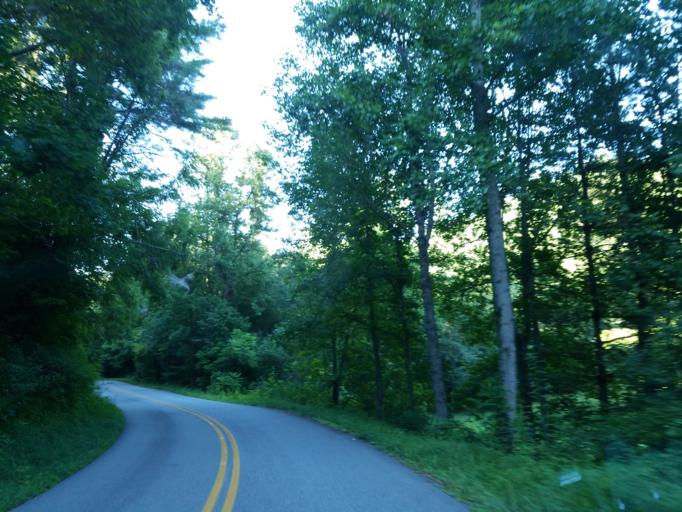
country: US
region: Georgia
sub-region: Union County
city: Blairsville
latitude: 34.7633
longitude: -84.0973
